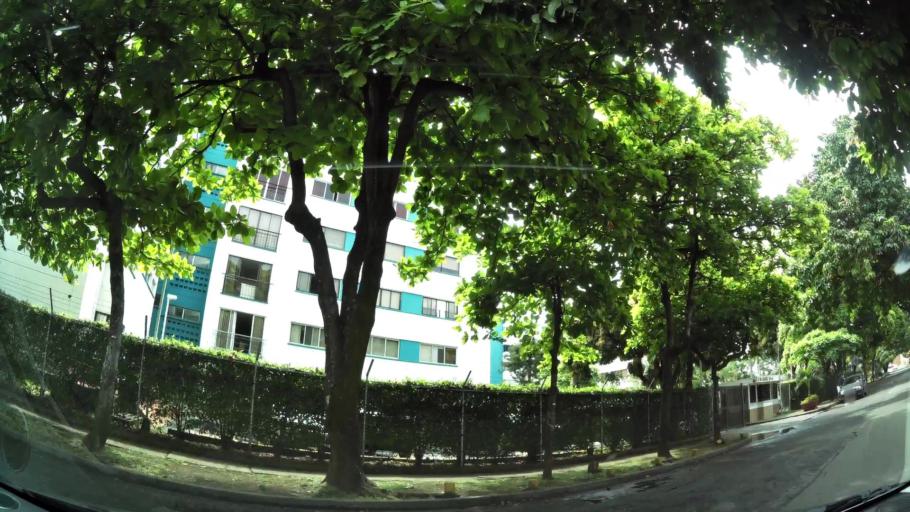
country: CO
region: Valle del Cauca
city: Cali
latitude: 3.3979
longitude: -76.5473
